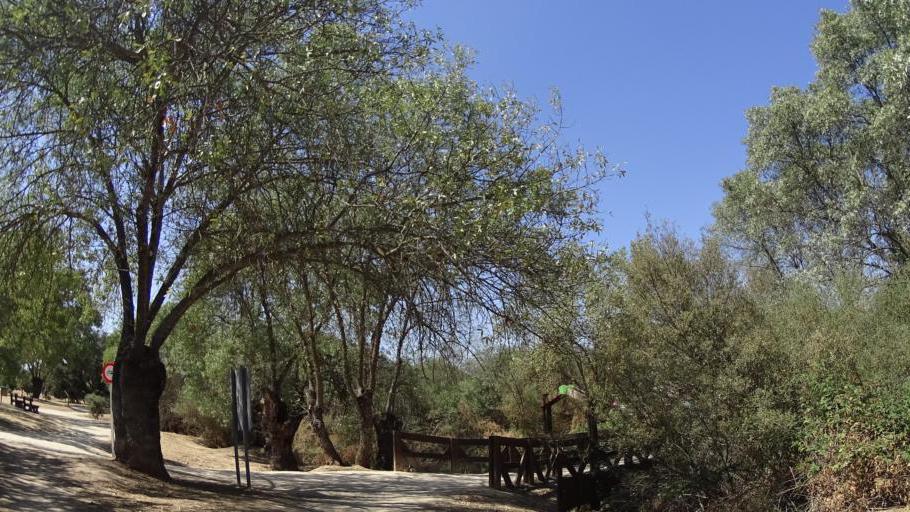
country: ES
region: Madrid
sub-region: Provincia de Madrid
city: Boadilla del Monte
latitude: 40.4143
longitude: -3.8632
